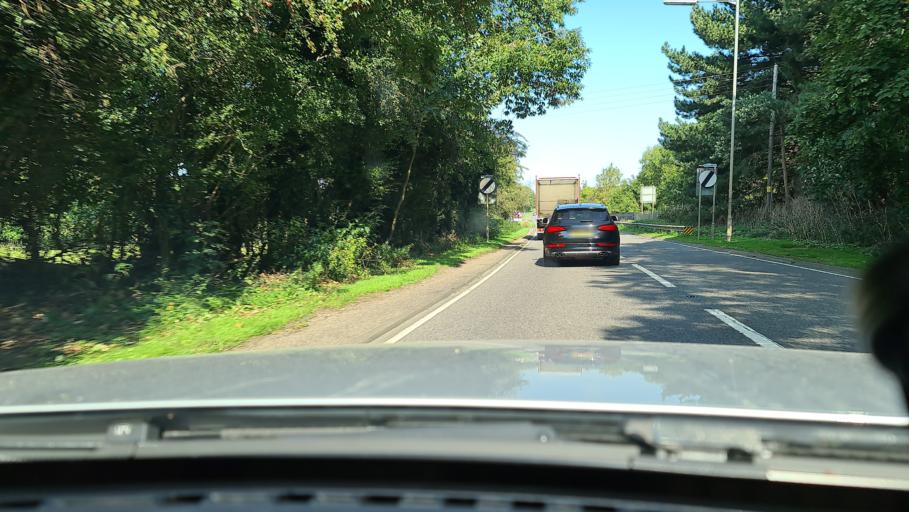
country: GB
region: England
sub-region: Northamptonshire
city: Daventry
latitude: 52.3383
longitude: -1.1737
